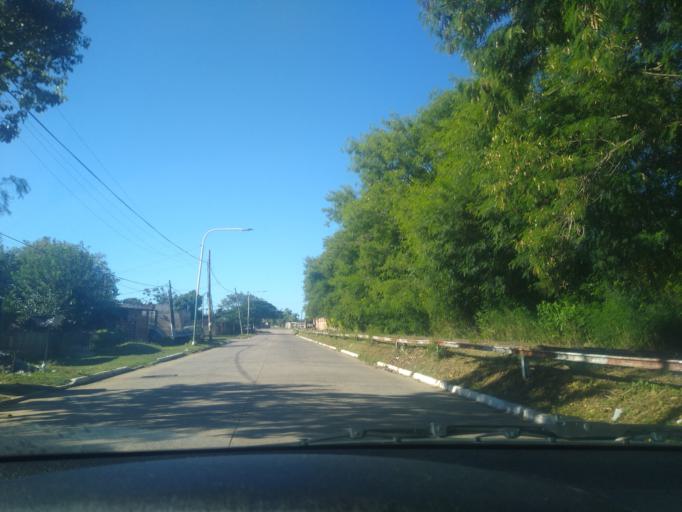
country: AR
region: Chaco
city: Puerto Vilelas
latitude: -27.5104
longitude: -58.9383
